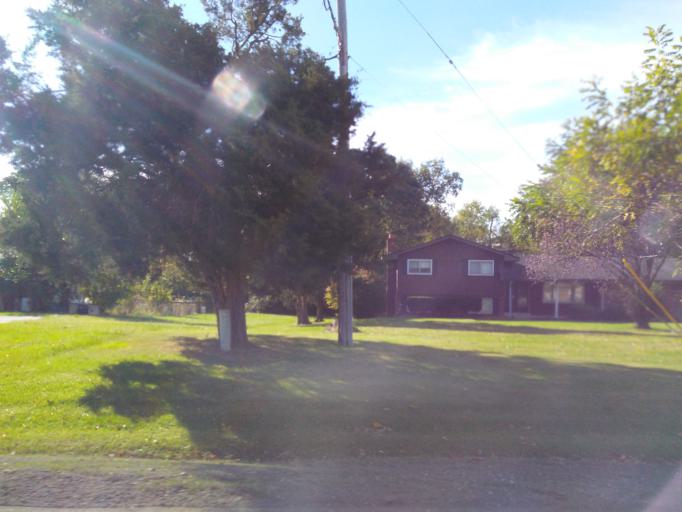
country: US
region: Illinois
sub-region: Madison County
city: Troy
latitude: 38.7177
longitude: -89.8798
